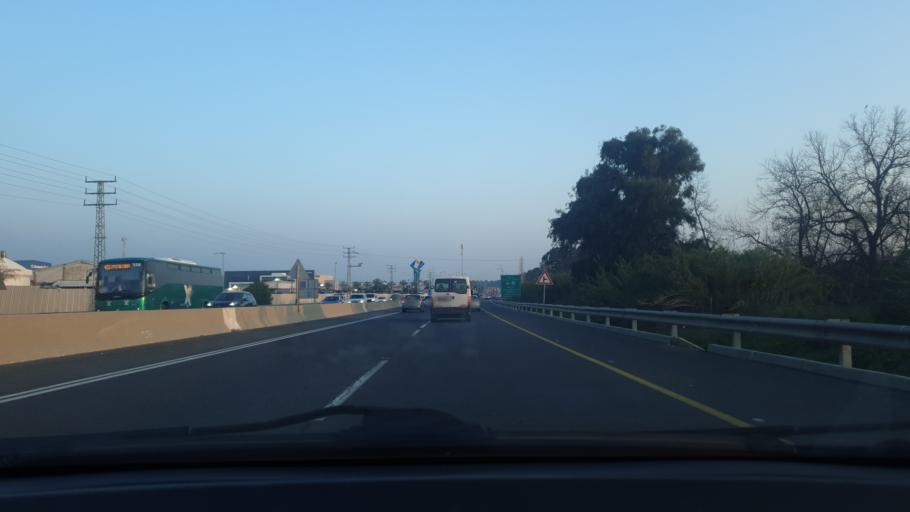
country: IL
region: Central District
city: Kefar Habad
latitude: 31.9670
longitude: 34.8459
